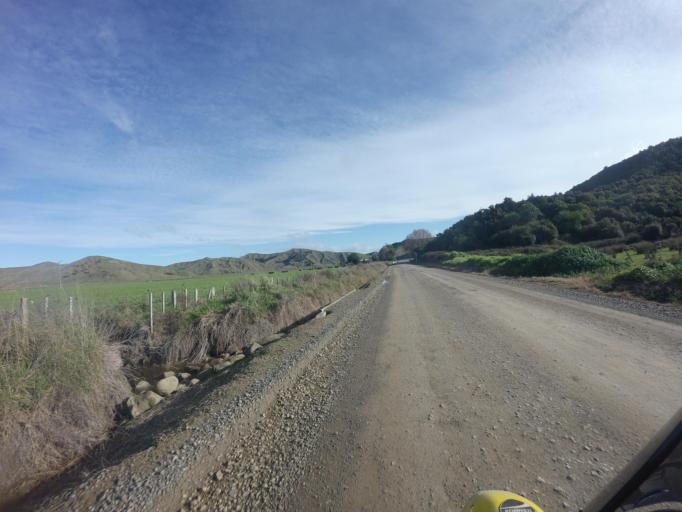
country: NZ
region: Hawke's Bay
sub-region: Wairoa District
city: Wairoa
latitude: -39.0283
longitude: 177.5847
